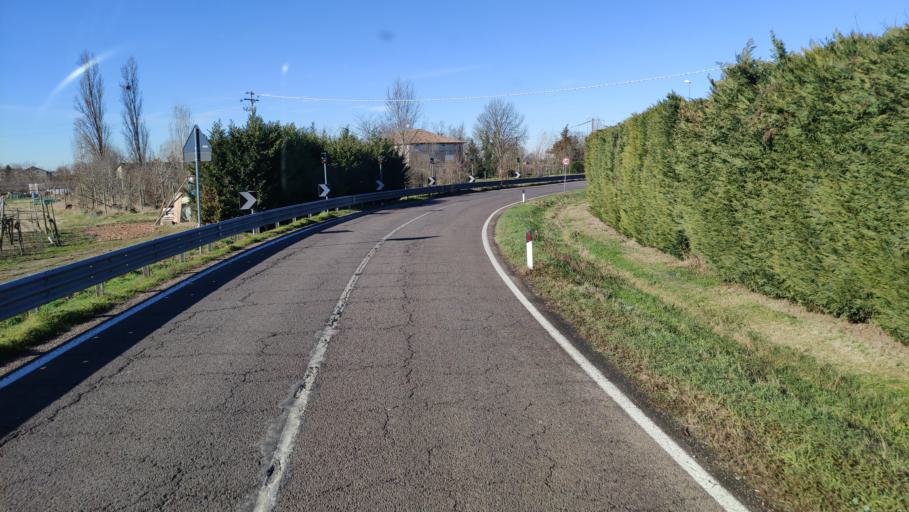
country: IT
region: Emilia-Romagna
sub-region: Provincia di Reggio Emilia
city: Rio Saliceto
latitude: 44.8081
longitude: 10.7831
